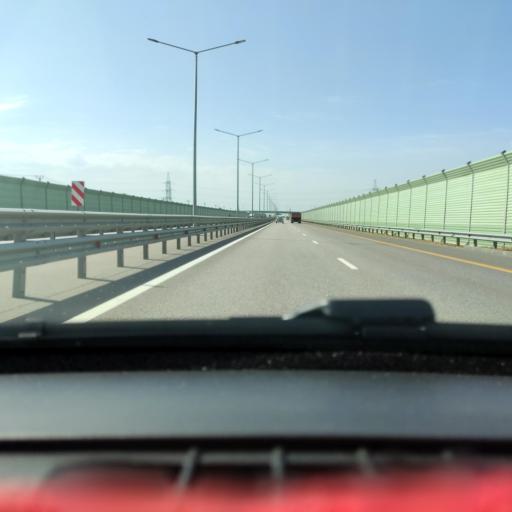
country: RU
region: Voronezj
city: Novaya Usman'
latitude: 51.6202
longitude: 39.3186
